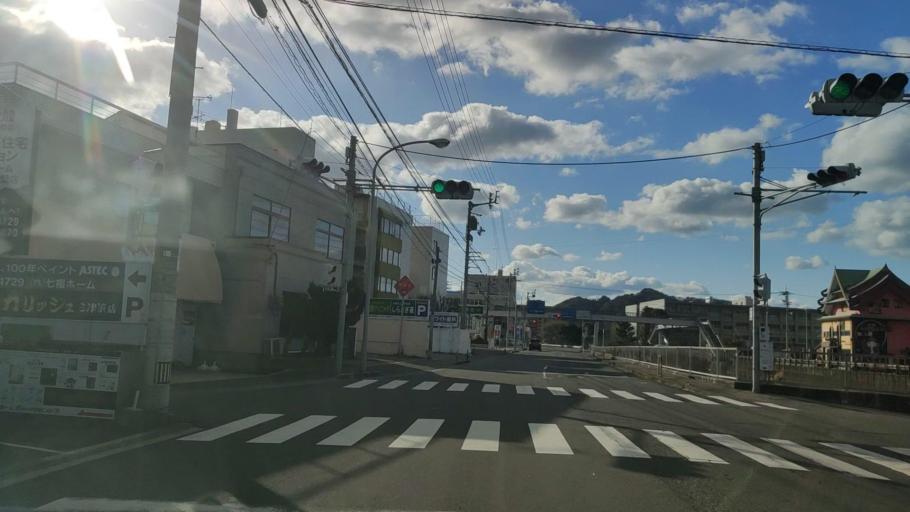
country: JP
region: Ehime
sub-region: Shikoku-chuo Shi
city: Matsuyama
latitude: 33.8588
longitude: 132.7193
